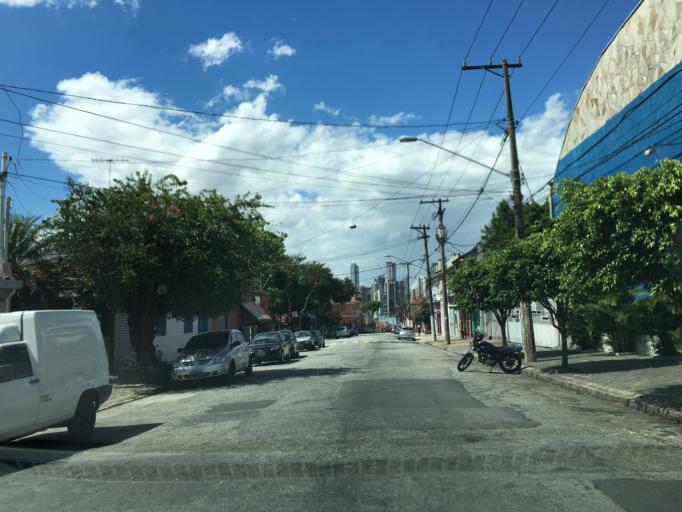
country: BR
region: Sao Paulo
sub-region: Sao Caetano Do Sul
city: Sao Caetano do Sul
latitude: -23.5701
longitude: -46.5664
